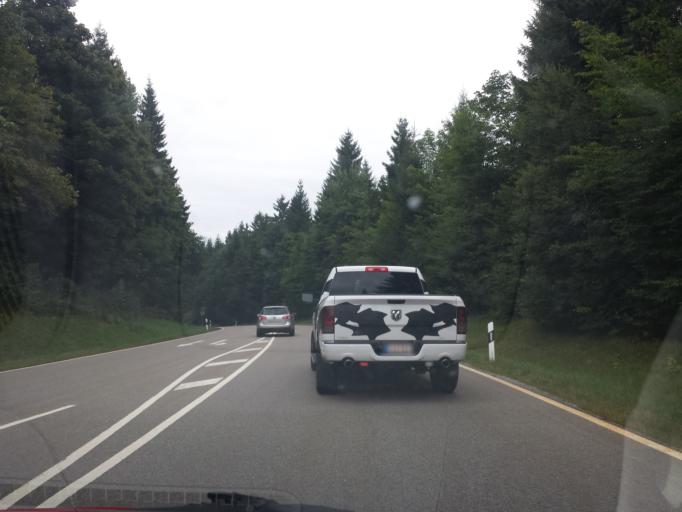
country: DE
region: Bavaria
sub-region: Lower Bavaria
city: Sankt Englmar
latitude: 49.0059
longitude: 12.8344
